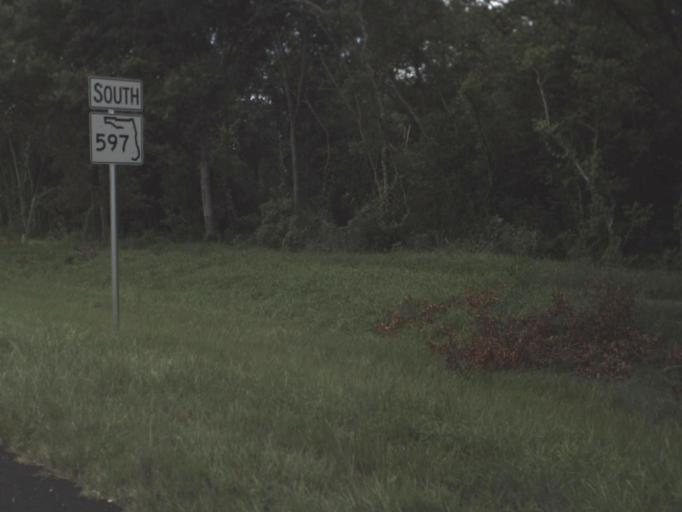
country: US
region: Florida
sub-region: Hillsborough County
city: Lutz
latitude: 28.1572
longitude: -82.4846
